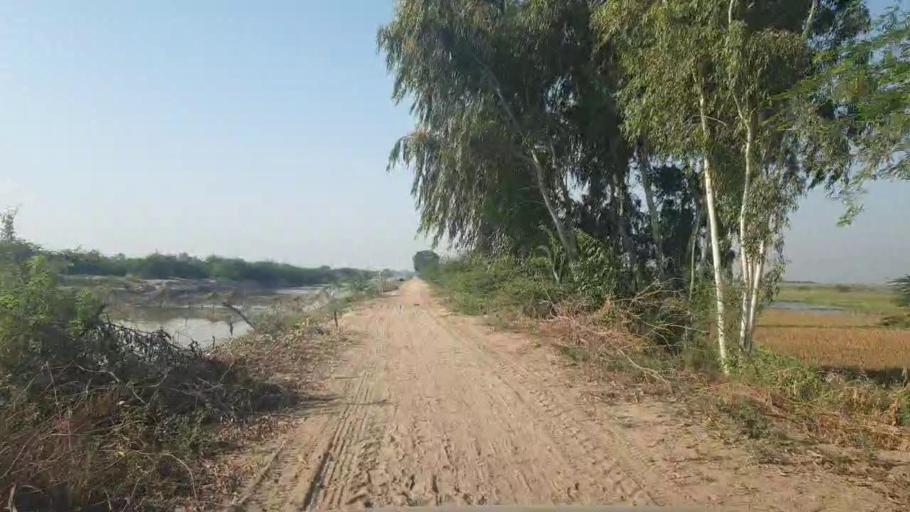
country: PK
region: Sindh
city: Tando Bago
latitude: 24.7283
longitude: 68.9264
